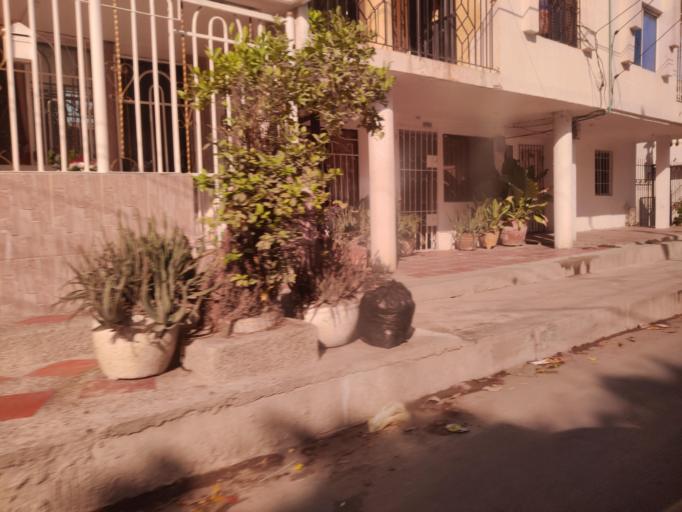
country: CO
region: Atlantico
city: Soledad
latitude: 10.9120
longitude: -74.8033
